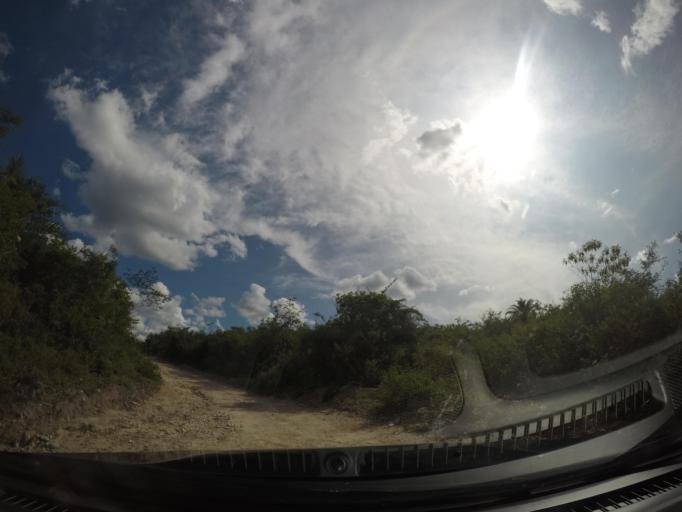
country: BR
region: Bahia
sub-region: Barra Da Estiva
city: Barra da Estiva
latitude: -13.1407
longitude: -41.5963
